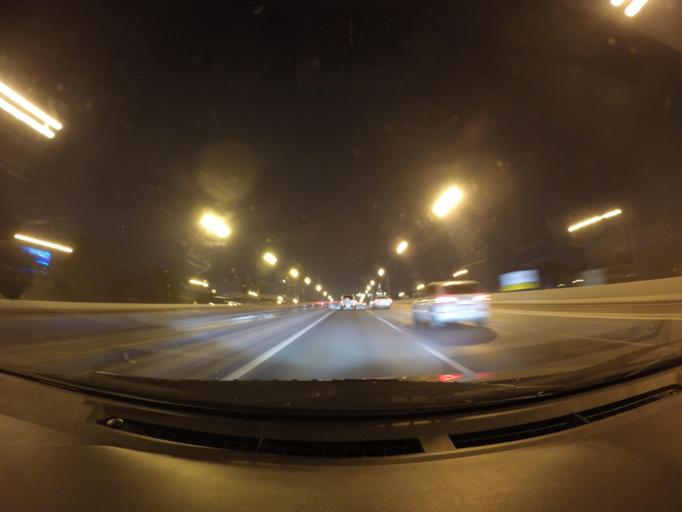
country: RU
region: Moskovskaya
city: Levoberezhnyy
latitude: 55.8407
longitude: 37.4803
